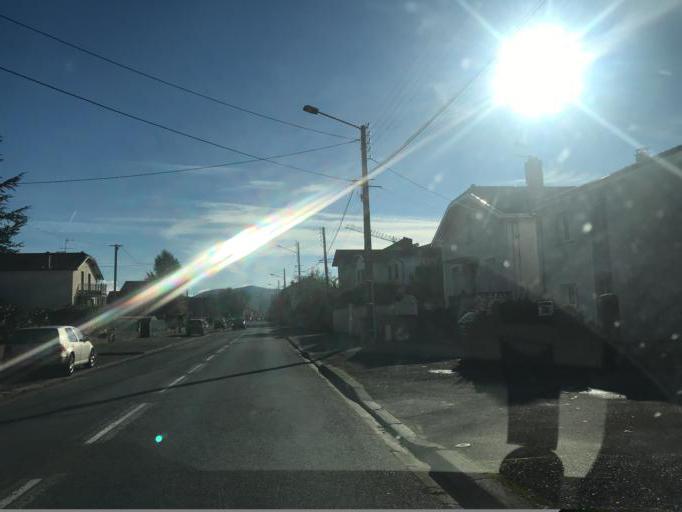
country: FR
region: Rhone-Alpes
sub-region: Departement de l'Ain
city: Amberieu-en-Bugey
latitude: 45.9703
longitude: 5.3531
